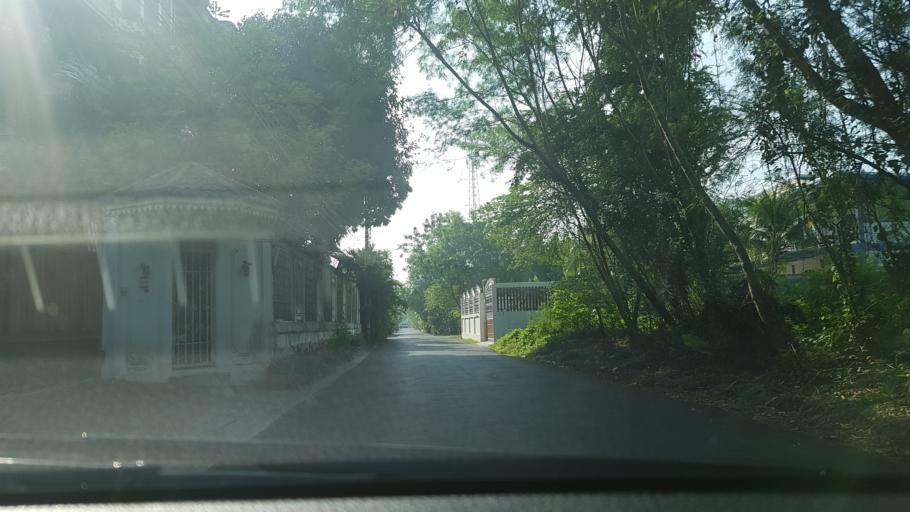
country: TH
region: Bangkok
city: Thawi Watthana
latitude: 13.7958
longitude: 100.3799
